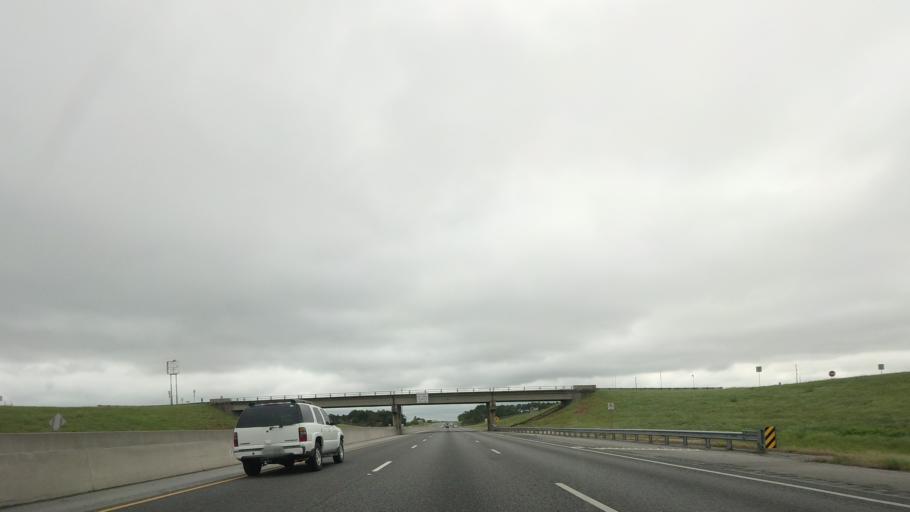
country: US
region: Georgia
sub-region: Turner County
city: Ashburn
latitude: 31.6273
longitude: -83.5770
